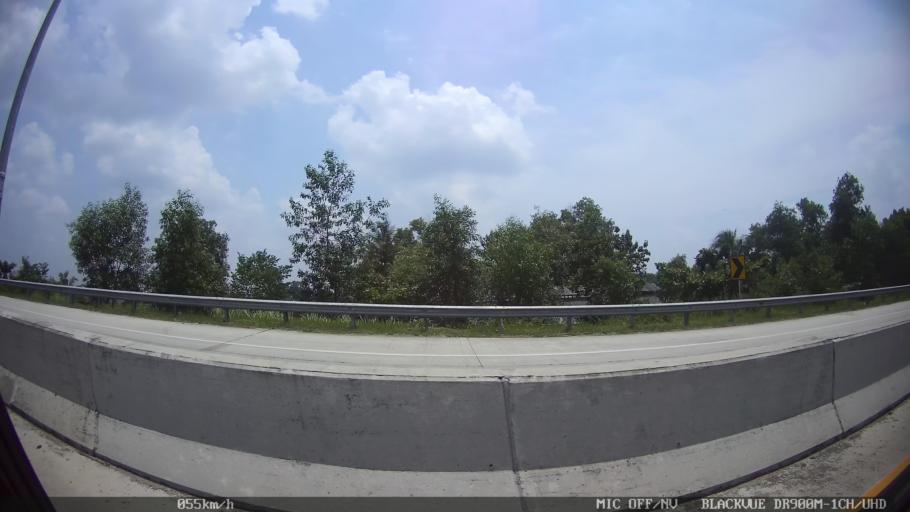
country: ID
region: Lampung
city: Natar
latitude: -5.2812
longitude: 105.2001
